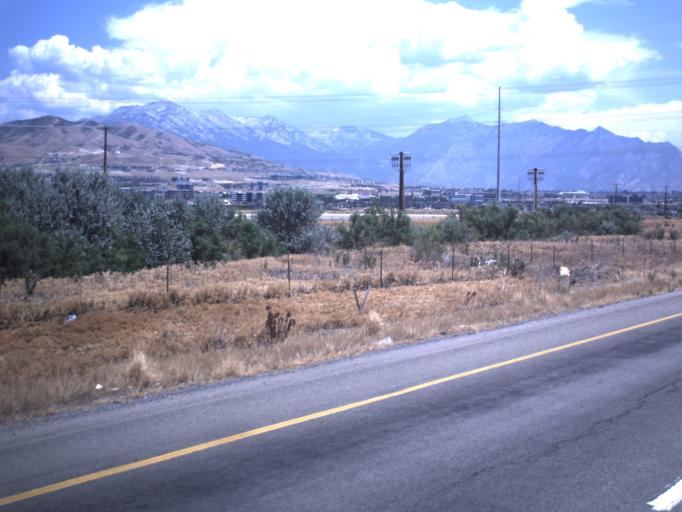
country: US
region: Utah
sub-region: Utah County
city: Saratoga Springs
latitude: 40.4126
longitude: -111.9119
